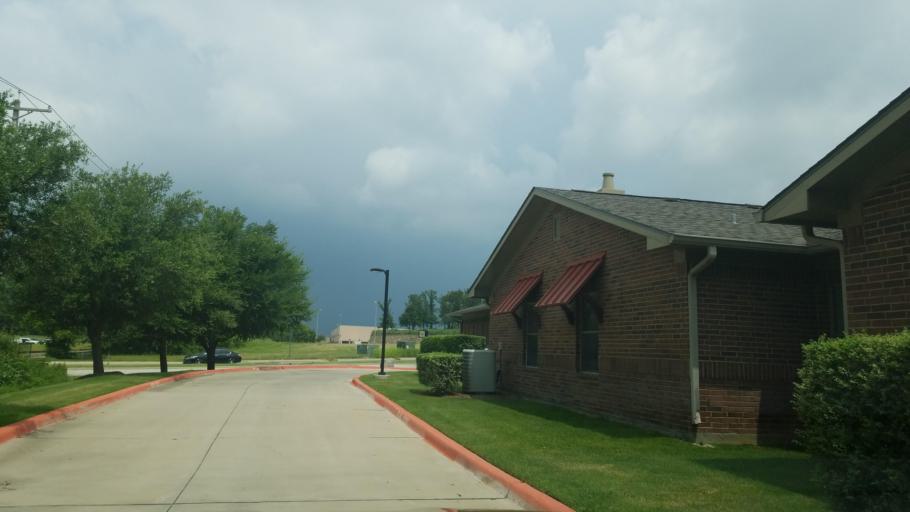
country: US
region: Texas
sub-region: Denton County
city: Corinth
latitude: 33.1853
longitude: -97.0956
